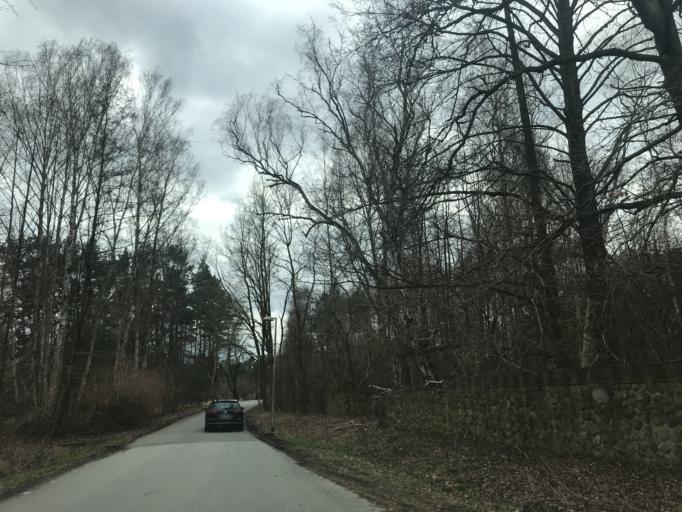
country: DE
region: Brandenburg
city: Zossen
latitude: 52.1443
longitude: 13.4741
